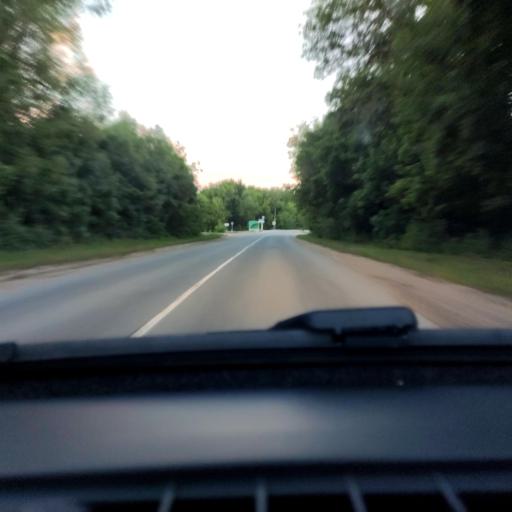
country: RU
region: Lipetsk
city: Zadonsk
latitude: 52.2976
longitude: 38.8509
